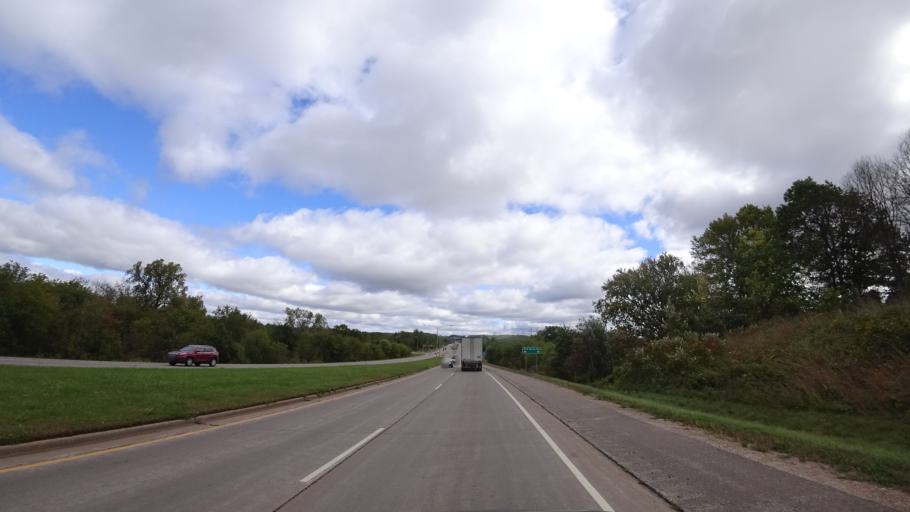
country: US
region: Wisconsin
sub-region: Eau Claire County
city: Eau Claire
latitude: 44.8412
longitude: -91.5110
